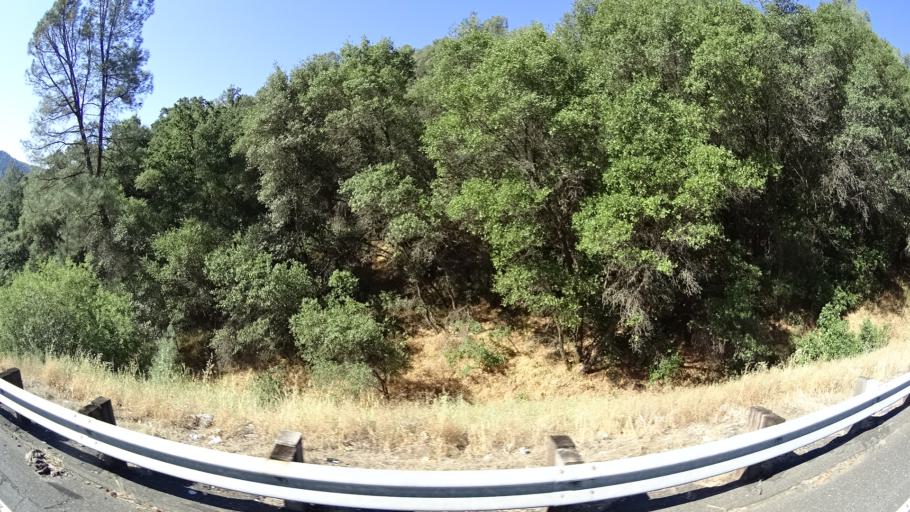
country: US
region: California
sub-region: Tuolumne County
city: Columbia
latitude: 38.0448
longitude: -120.4638
